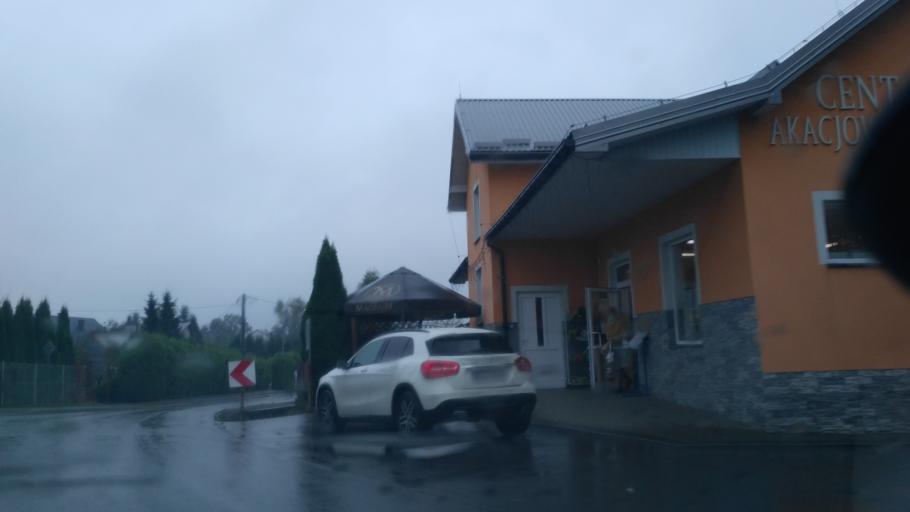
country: PL
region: Subcarpathian Voivodeship
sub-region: Powiat krosnienski
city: Korczyna
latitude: 49.7042
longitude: 21.8121
